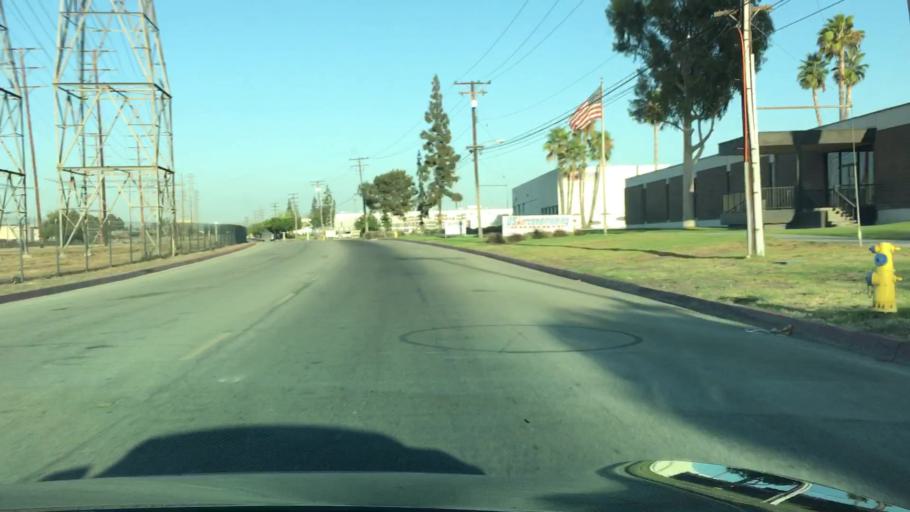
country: US
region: California
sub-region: Los Angeles County
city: La Puente
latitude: 34.0073
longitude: -117.9367
